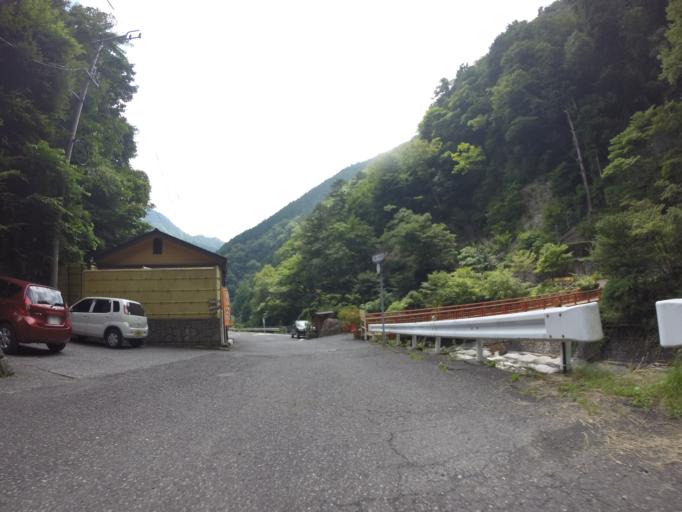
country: JP
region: Shizuoka
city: Fujinomiya
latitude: 35.3061
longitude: 138.3380
